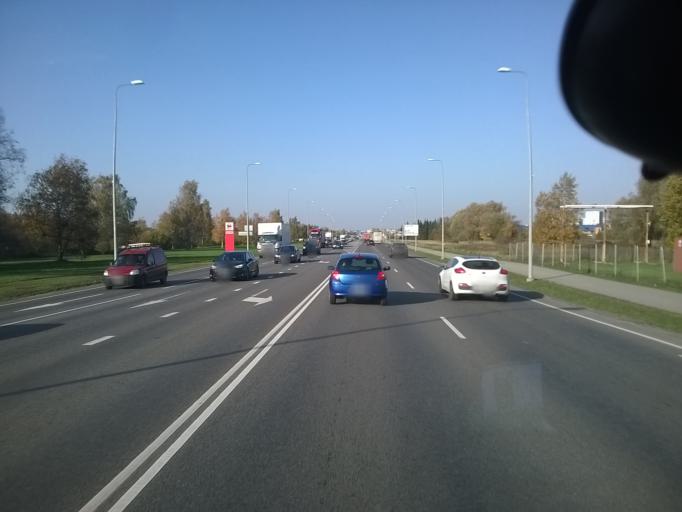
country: EE
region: Harju
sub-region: Tallinna linn
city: Tallinn
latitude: 59.4085
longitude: 24.8059
